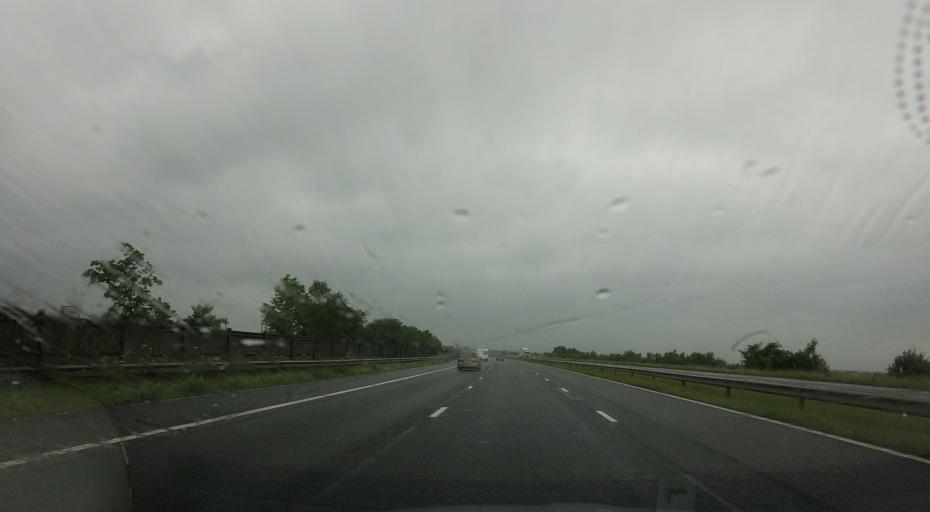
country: GB
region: Scotland
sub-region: Dumfries and Galloway
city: Gretna
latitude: 54.9714
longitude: -3.0047
